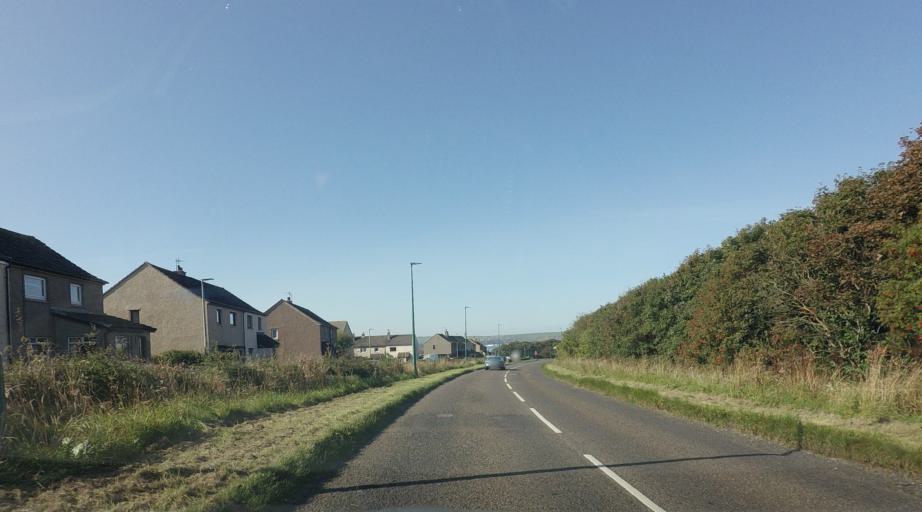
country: GB
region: Scotland
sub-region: Highland
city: Thurso
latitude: 58.5944
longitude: -3.5038
